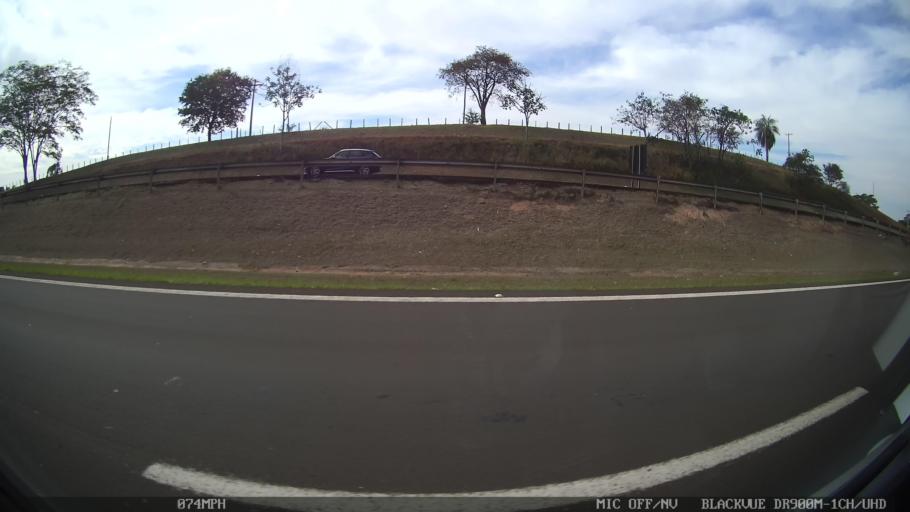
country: BR
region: Sao Paulo
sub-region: Matao
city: Matao
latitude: -21.5770
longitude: -48.4558
